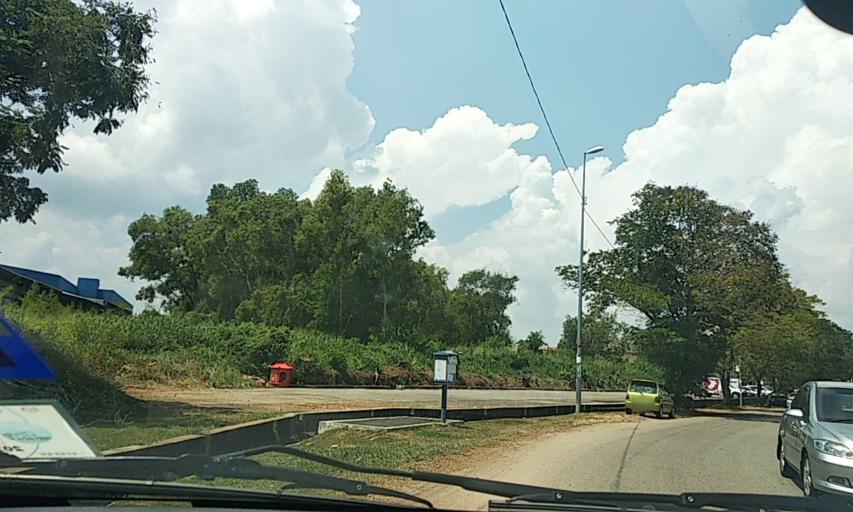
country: MY
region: Kedah
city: Sungai Petani
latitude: 5.6227
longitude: 100.4739
